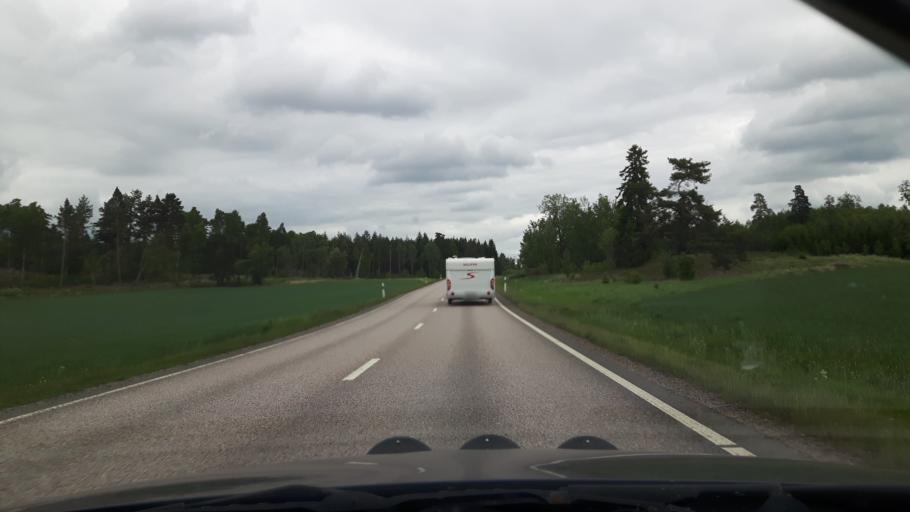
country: SE
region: Soedermanland
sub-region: Strangnas Kommun
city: Akers Styckebruk
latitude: 59.2616
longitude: 16.9468
